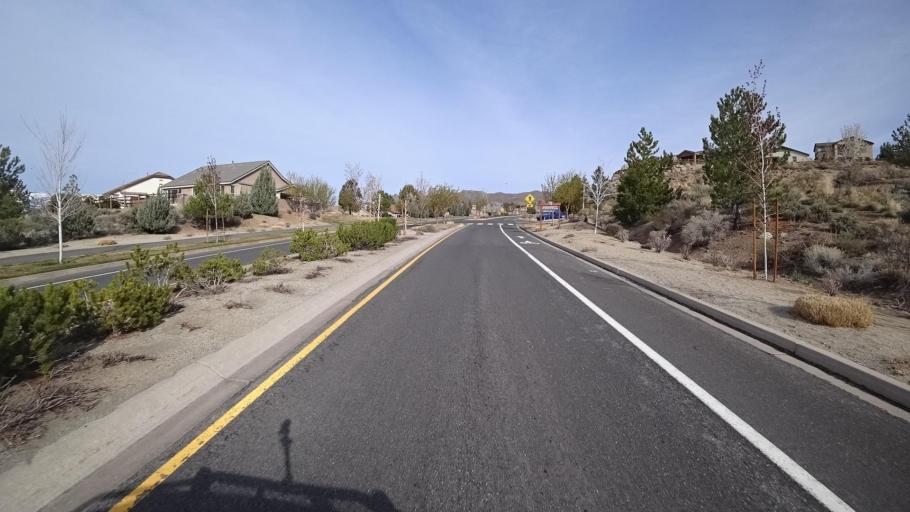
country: US
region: Nevada
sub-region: Washoe County
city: Mogul
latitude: 39.5264
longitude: -119.9478
